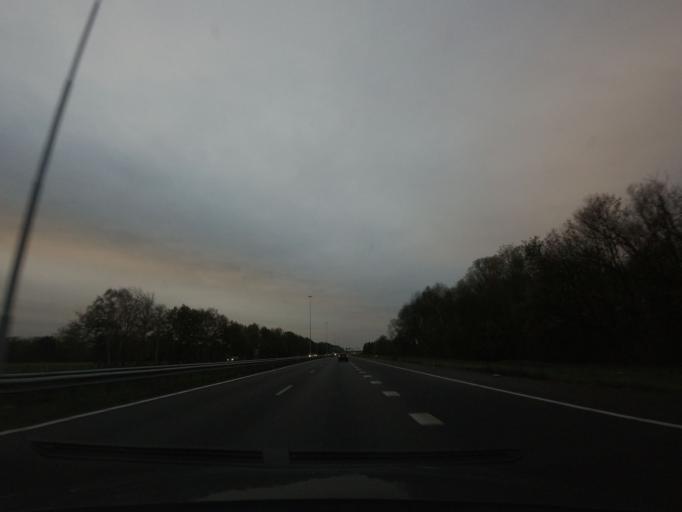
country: NL
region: North Brabant
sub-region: Gemeente Breda
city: Hoge Vucht
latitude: 51.5772
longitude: 4.8235
